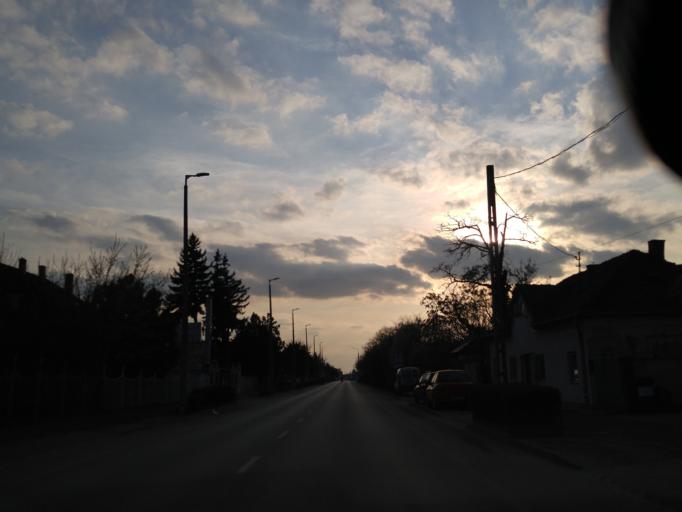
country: HU
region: Somogy
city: Siofok
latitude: 46.9038
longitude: 18.0429
